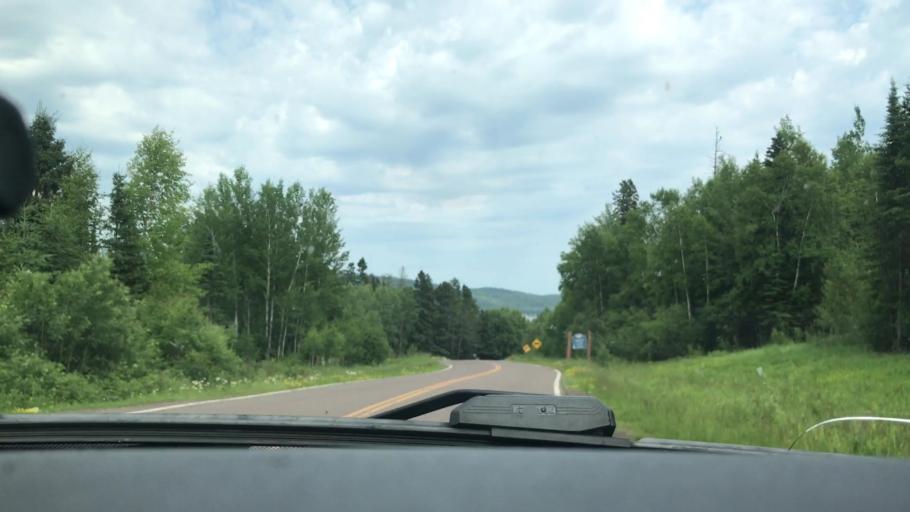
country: CA
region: Ontario
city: Neebing
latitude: 47.9647
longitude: -89.6881
